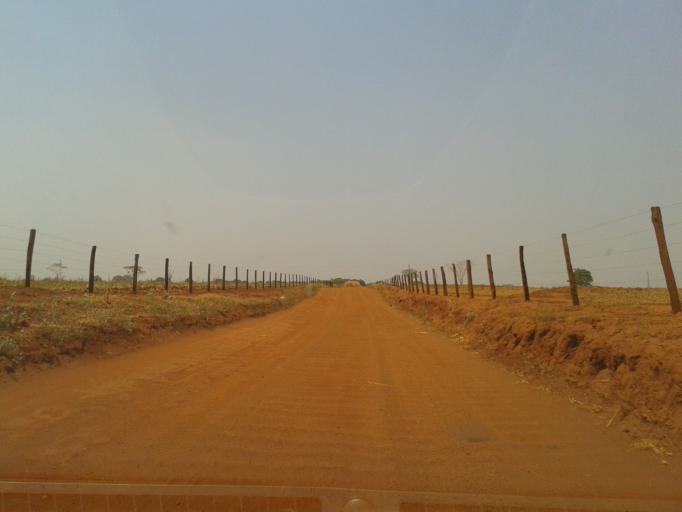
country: BR
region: Minas Gerais
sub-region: Centralina
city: Centralina
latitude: -18.7161
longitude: -49.2158
